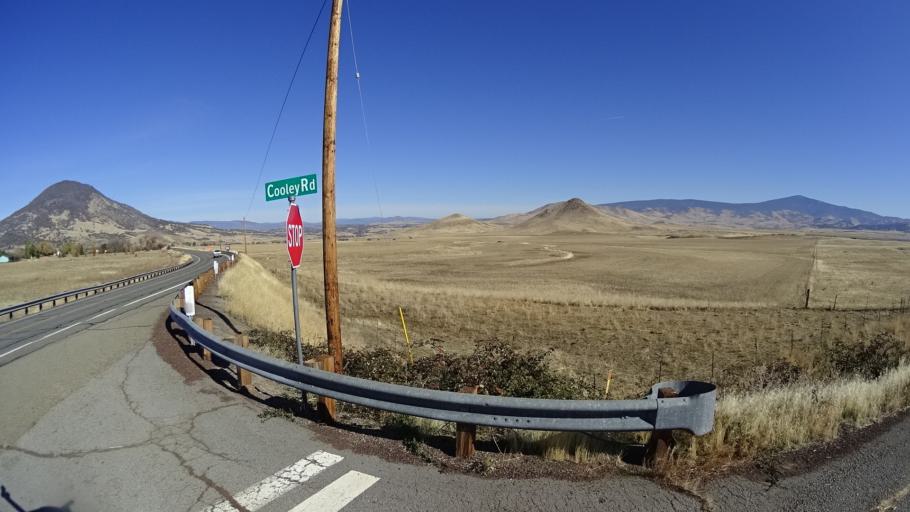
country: US
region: California
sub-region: Siskiyou County
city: Montague
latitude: 41.8075
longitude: -122.4986
